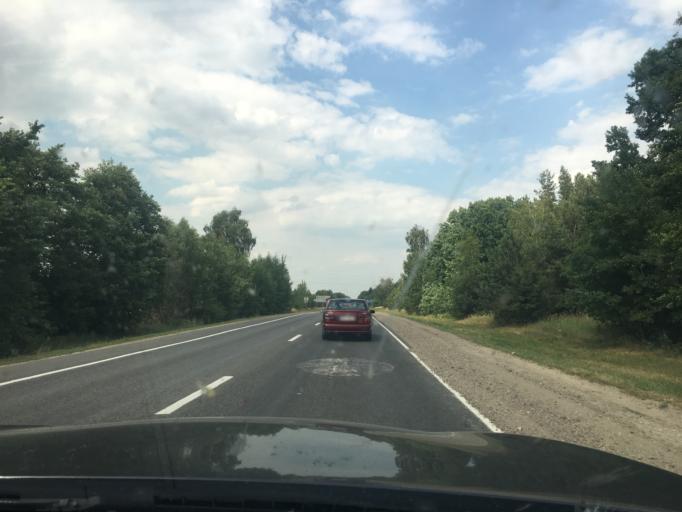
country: BY
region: Brest
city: Brest
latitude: 52.1544
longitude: 23.6945
